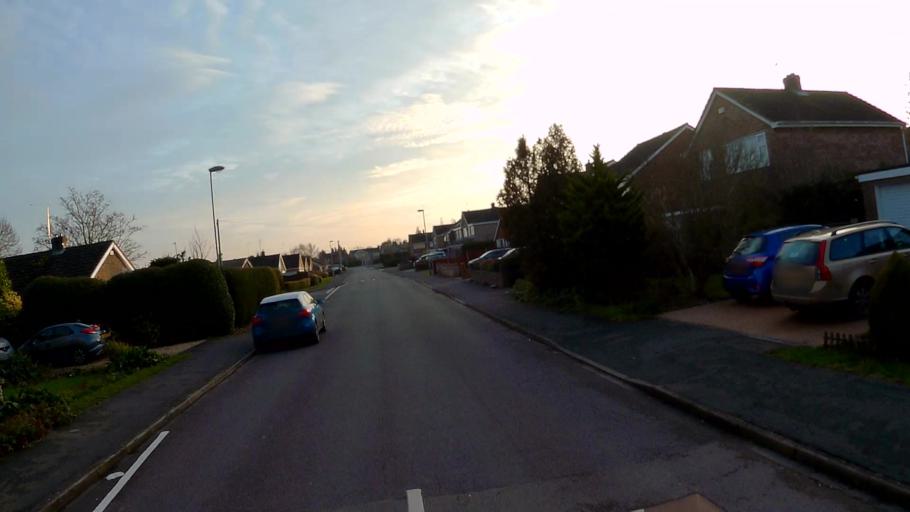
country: GB
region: England
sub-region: Lincolnshire
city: Bourne
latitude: 52.7683
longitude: -0.3928
